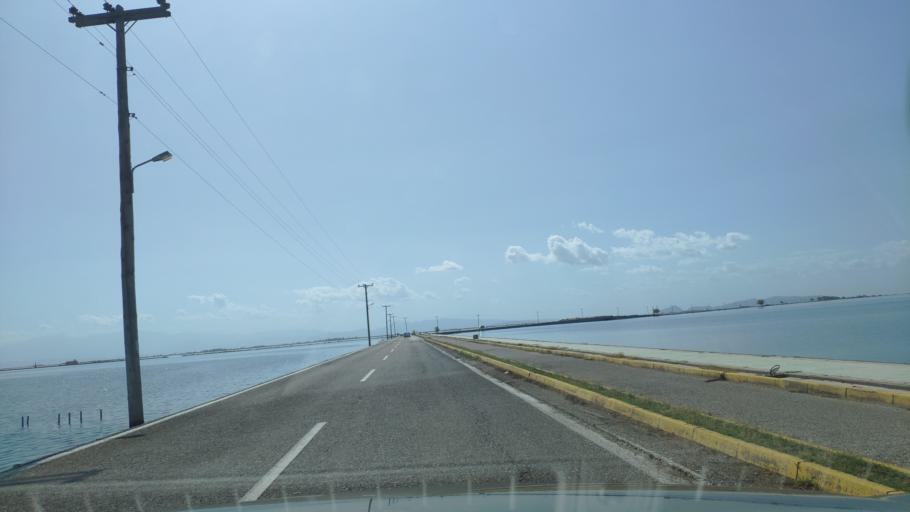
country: GR
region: West Greece
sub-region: Nomos Aitolias kai Akarnanias
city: Mesolongi
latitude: 38.3541
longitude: 21.4292
